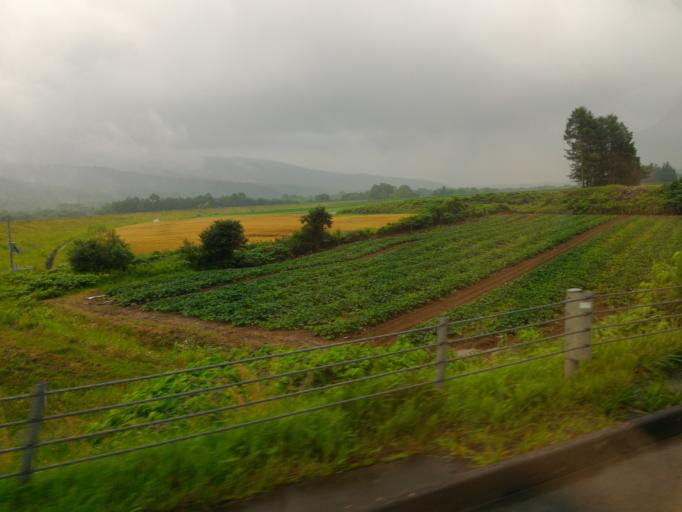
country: JP
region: Hokkaido
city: Nayoro
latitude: 44.5902
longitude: 142.3060
